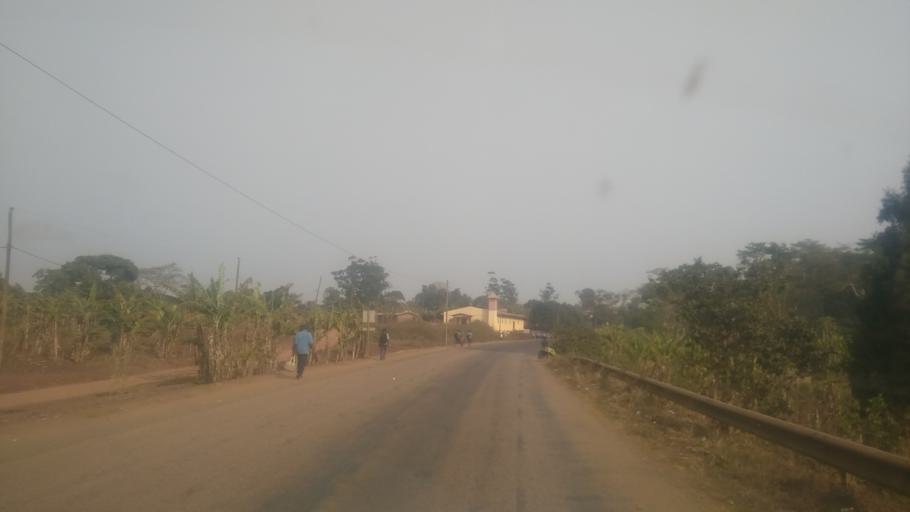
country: CM
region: West
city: Tonga
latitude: 5.0659
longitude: 10.6848
